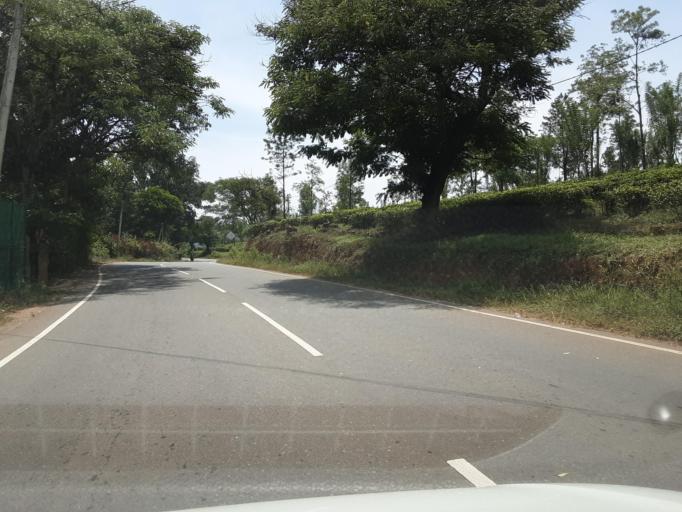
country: LK
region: Central
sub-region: Nuwara Eliya District
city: Nuwara Eliya
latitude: 6.9445
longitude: 80.9144
